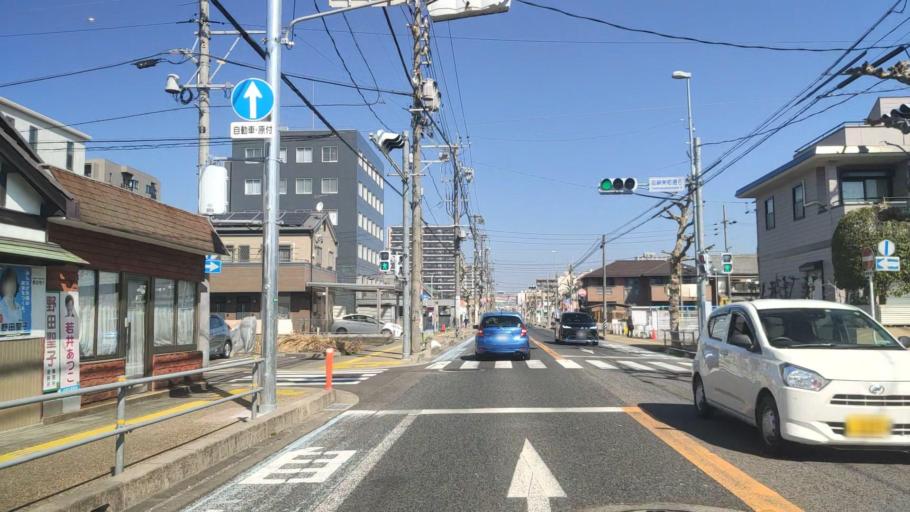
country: JP
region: Gifu
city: Gifu-shi
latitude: 35.4019
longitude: 136.7536
